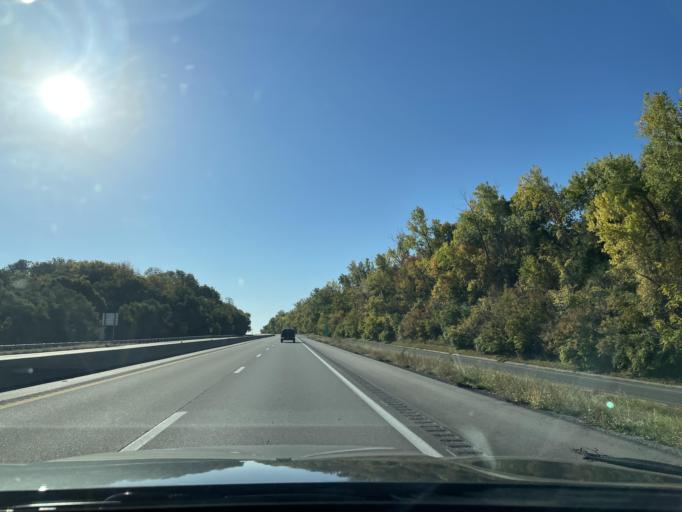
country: US
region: Missouri
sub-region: Buchanan County
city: Saint Joseph
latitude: 39.7807
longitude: -94.8680
